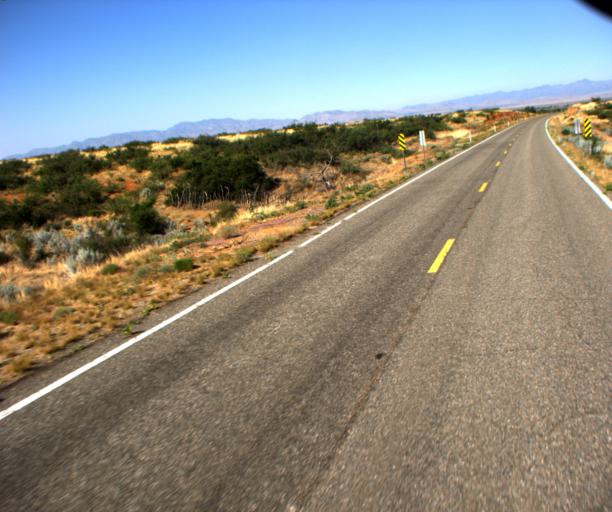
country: US
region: Arizona
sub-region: Graham County
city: Swift Trail Junction
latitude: 32.5892
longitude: -109.9099
